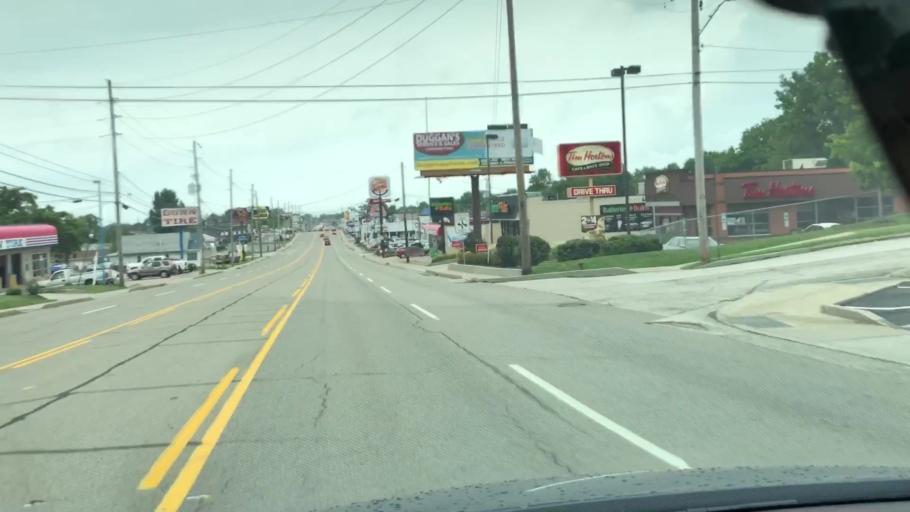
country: US
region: Pennsylvania
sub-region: Erie County
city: Erie
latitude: 42.0900
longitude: -80.0854
